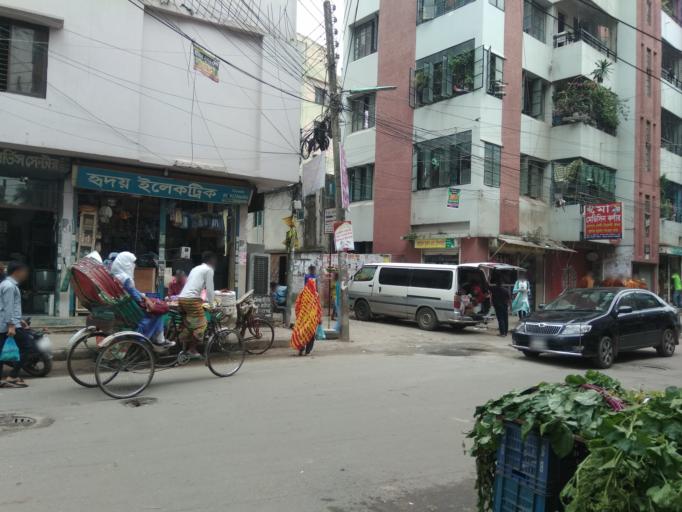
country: BD
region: Dhaka
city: Azimpur
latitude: 23.8057
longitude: 90.3731
